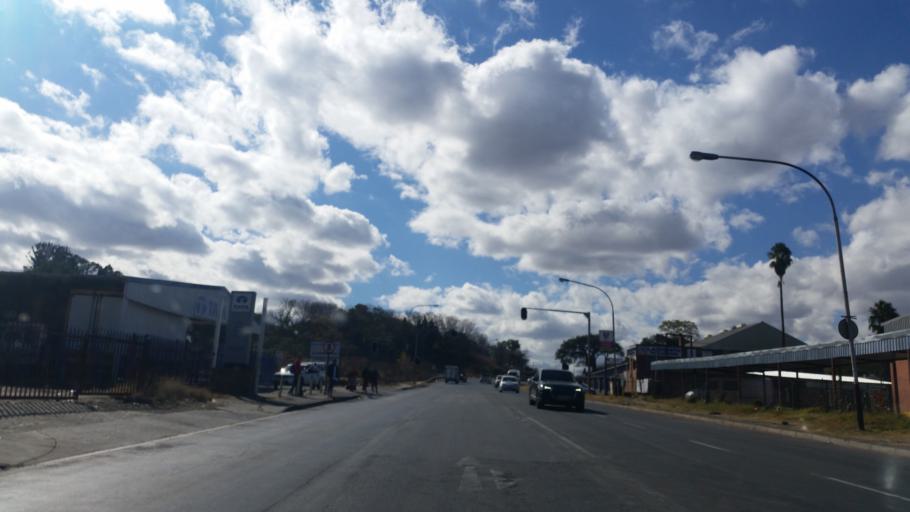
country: ZA
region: KwaZulu-Natal
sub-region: uThukela District Municipality
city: Ladysmith
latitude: -28.5511
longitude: 29.7901
